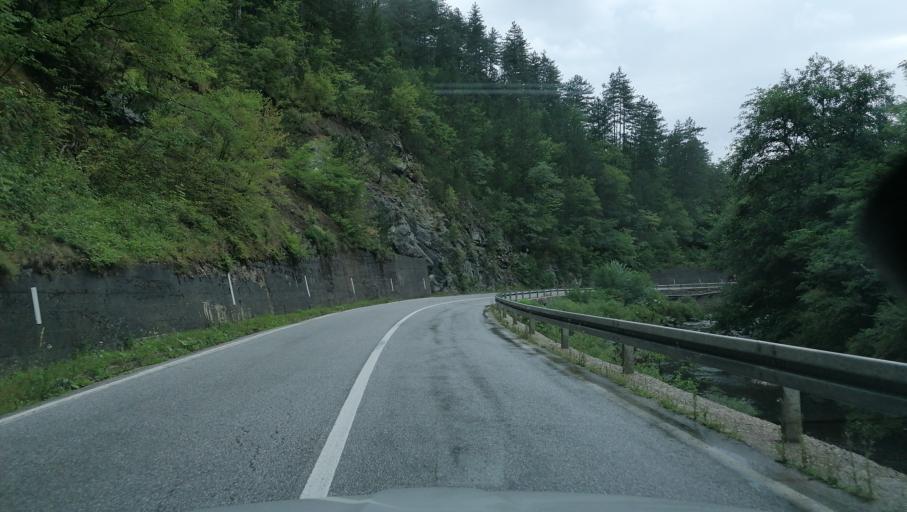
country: RS
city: Durici
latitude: 43.7755
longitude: 19.3774
